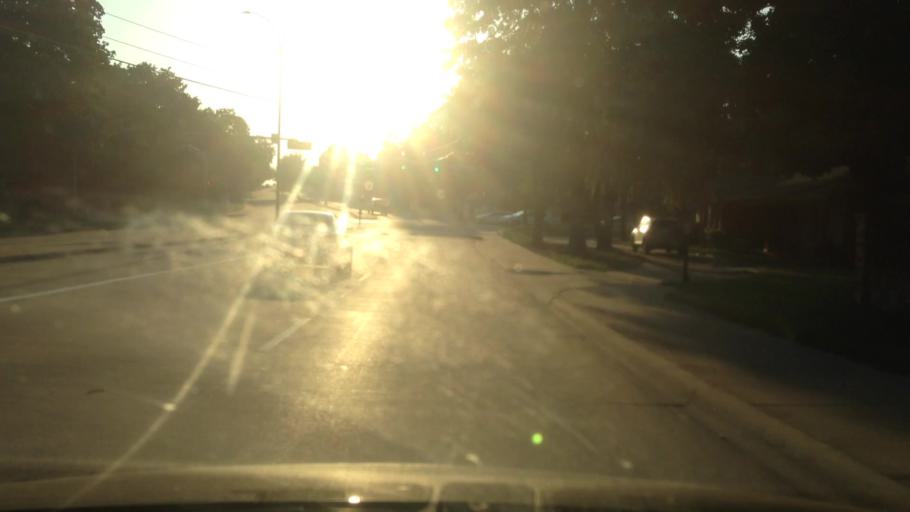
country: US
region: Texas
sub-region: Tarrant County
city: Dalworthington Gardens
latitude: 32.6490
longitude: -97.1661
